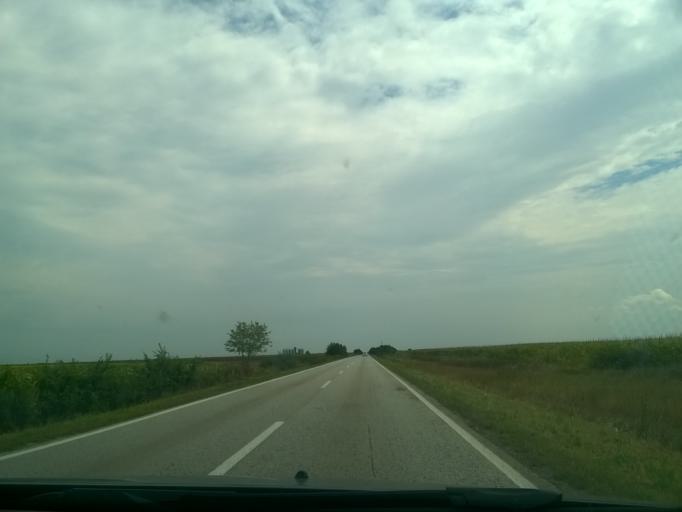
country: RS
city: Banatski Despotovac
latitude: 45.3822
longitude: 20.6520
